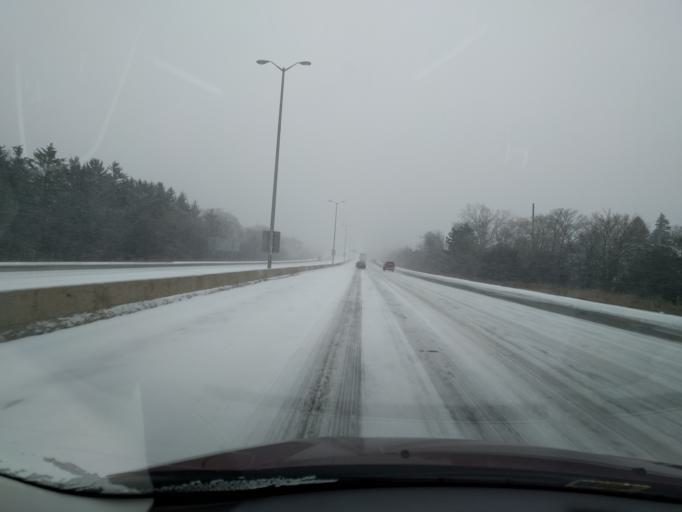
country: US
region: Wisconsin
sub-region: Waukesha County
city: Butler
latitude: 43.1419
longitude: -88.0412
